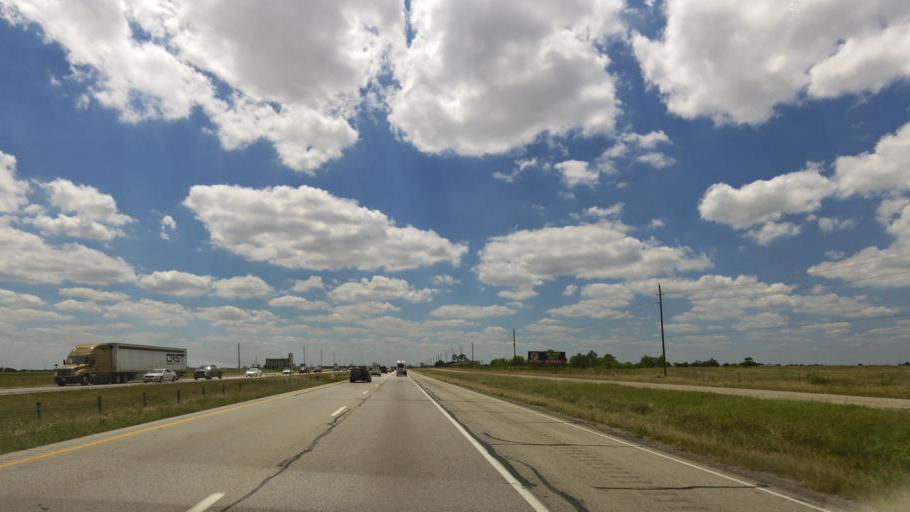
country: US
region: Texas
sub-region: Austin County
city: Sealy
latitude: 29.7559
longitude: -96.2420
